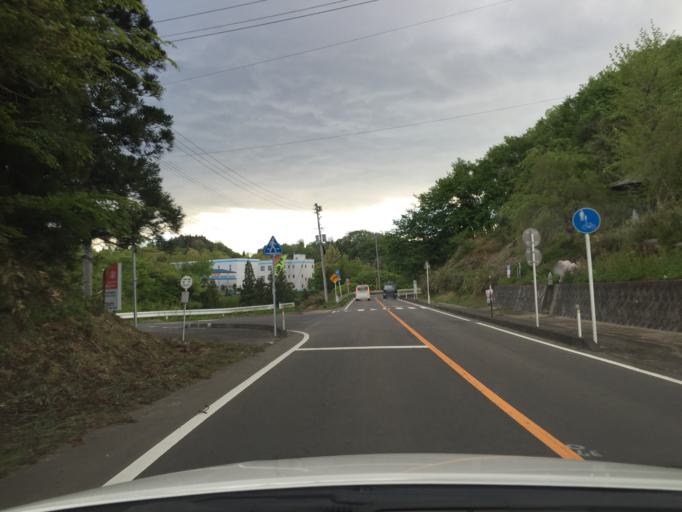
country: JP
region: Fukushima
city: Fukushima-shi
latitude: 37.6606
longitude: 140.5116
